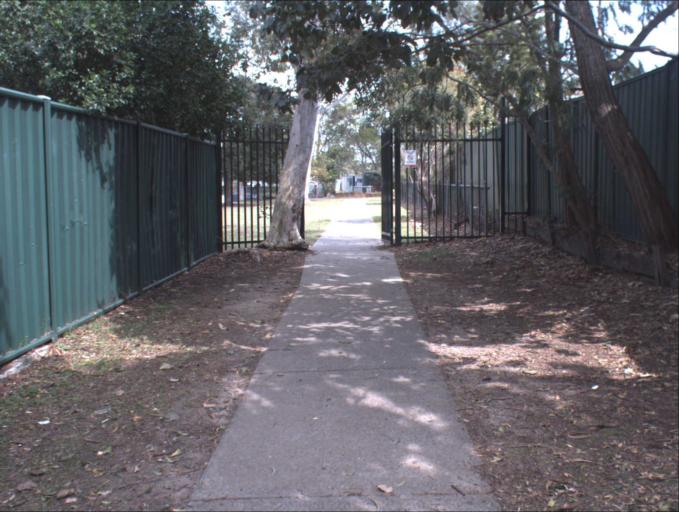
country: AU
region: Queensland
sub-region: Logan
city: Logan Reserve
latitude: -27.6868
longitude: 153.0915
